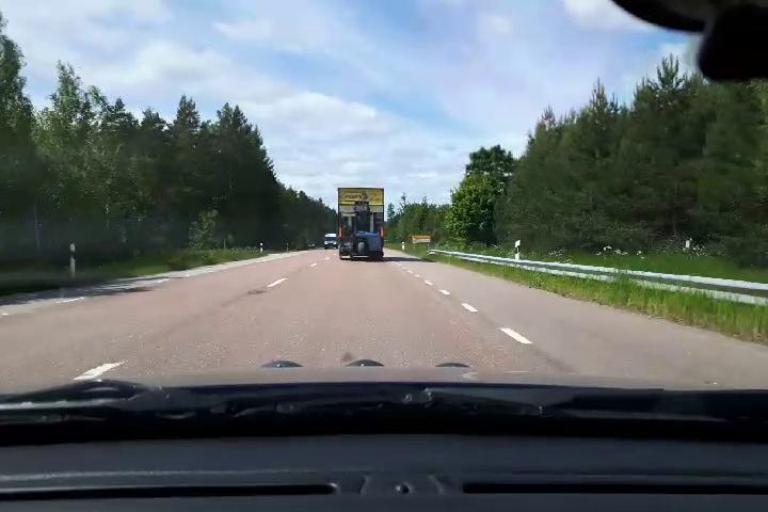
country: SE
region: Uppsala
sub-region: Osthammars Kommun
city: Bjorklinge
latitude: 60.1106
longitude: 17.5327
